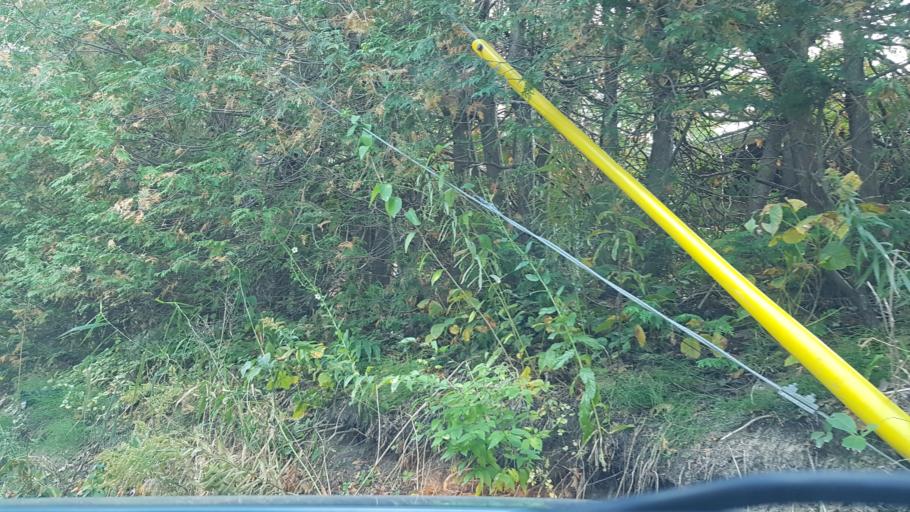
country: CA
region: Ontario
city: Lambton Shores
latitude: 43.3118
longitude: -81.7670
